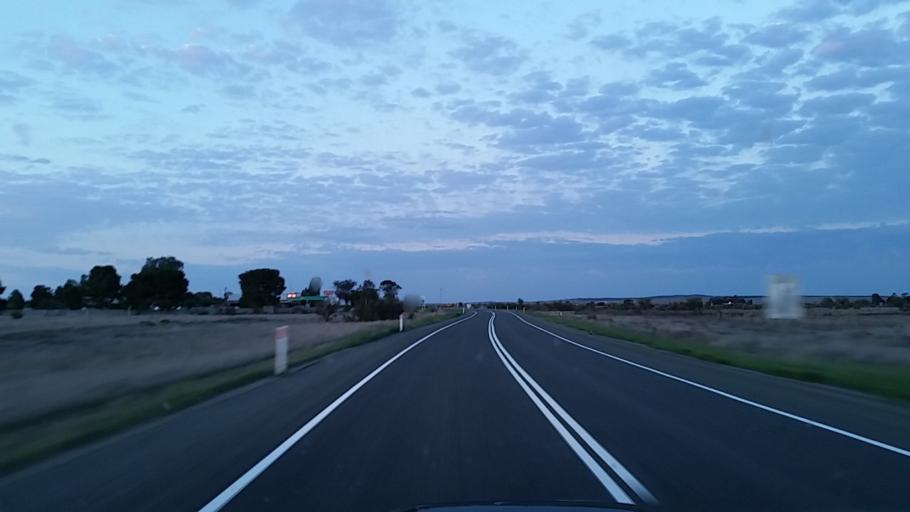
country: AU
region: South Australia
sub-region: Peterborough
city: Peterborough
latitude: -33.1558
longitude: 138.9207
